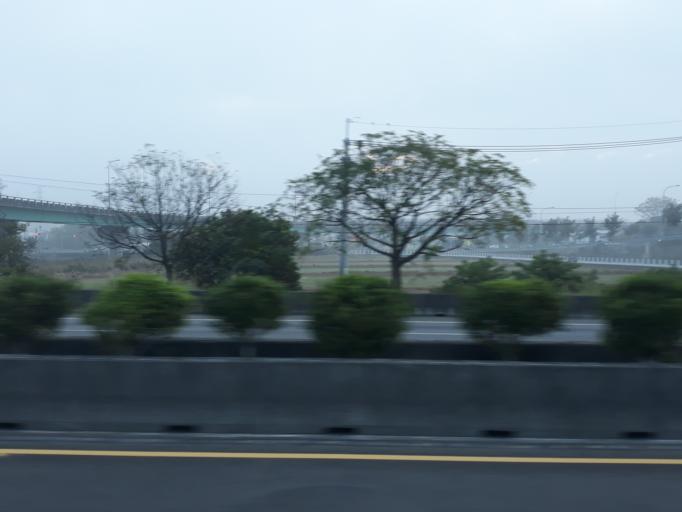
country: TW
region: Taiwan
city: Fengyuan
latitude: 24.3133
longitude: 120.7019
